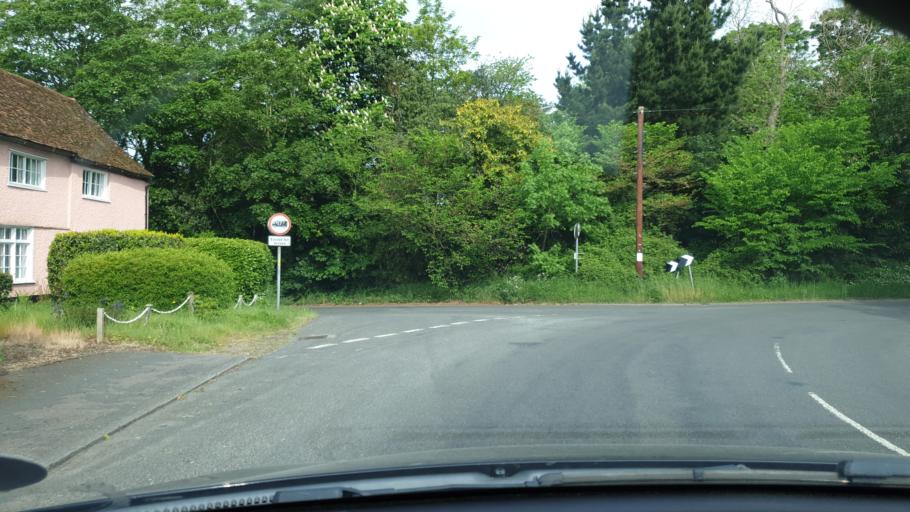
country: GB
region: England
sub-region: Essex
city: Great Bentley
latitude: 51.8752
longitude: 1.1120
